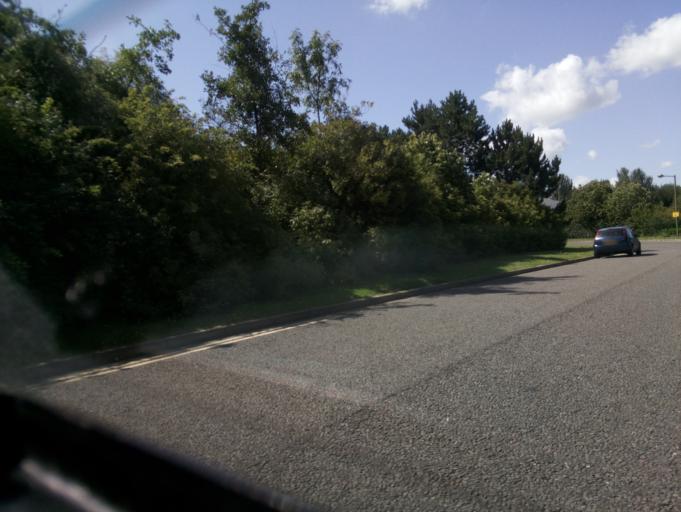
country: GB
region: England
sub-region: Milton Keynes
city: Loughton
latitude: 52.0239
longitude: -0.7731
